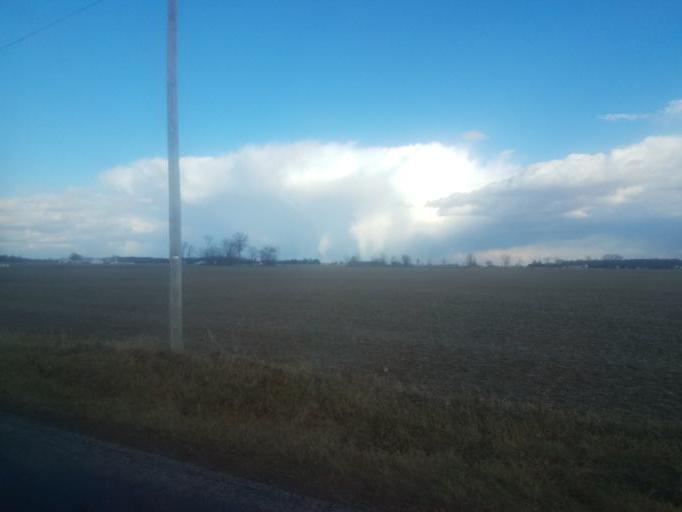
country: US
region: Ohio
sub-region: Marion County
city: Prospect
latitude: 40.4743
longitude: -83.1321
